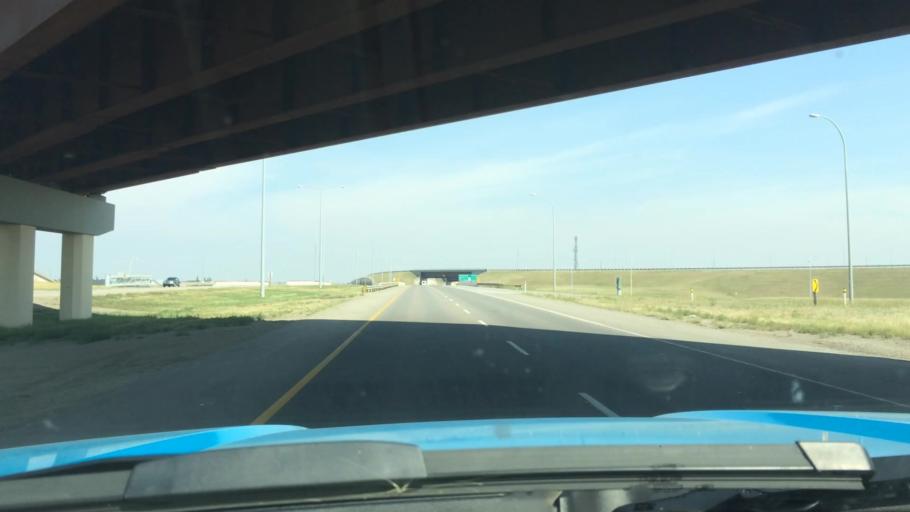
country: CA
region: Alberta
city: Okotoks
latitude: 50.8994
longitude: -113.9787
